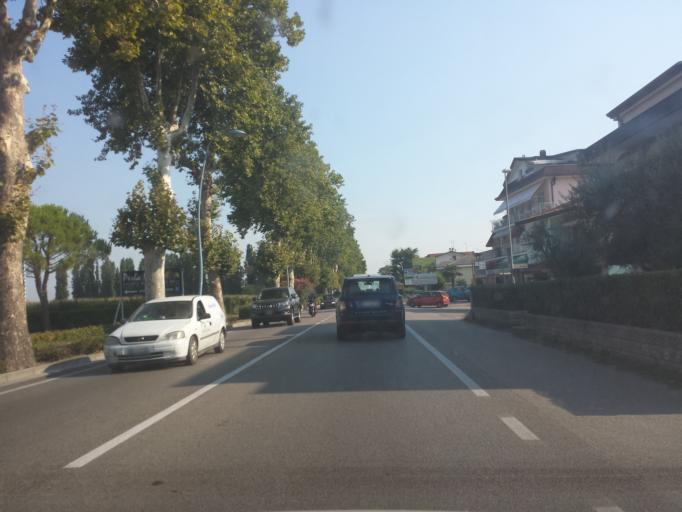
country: IT
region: Veneto
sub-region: Provincia di Venezia
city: Iesolo
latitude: 45.5246
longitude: 12.6402
